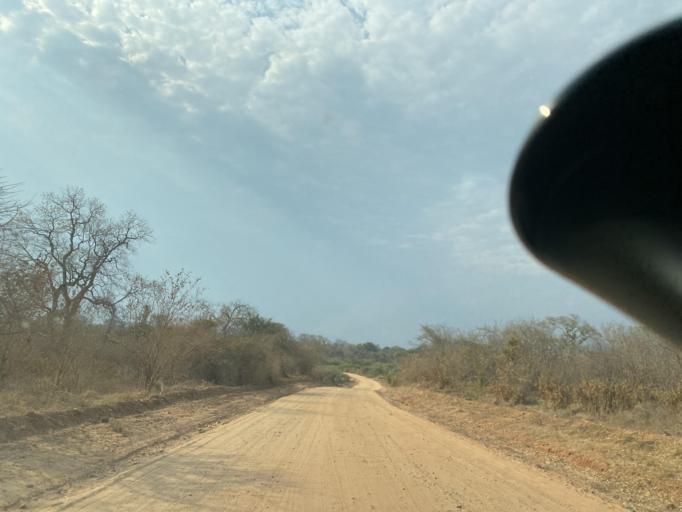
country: ZW
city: Chirundu
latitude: -15.9348
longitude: 28.9295
